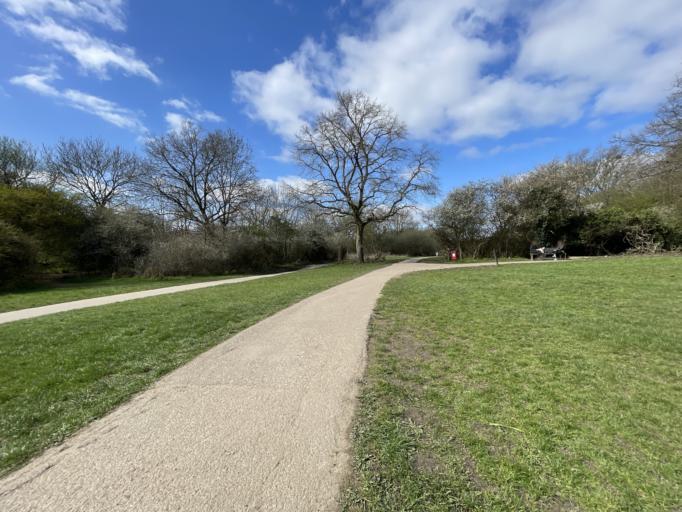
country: GB
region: England
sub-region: Greater London
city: Barnet
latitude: 51.6378
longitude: -0.1857
